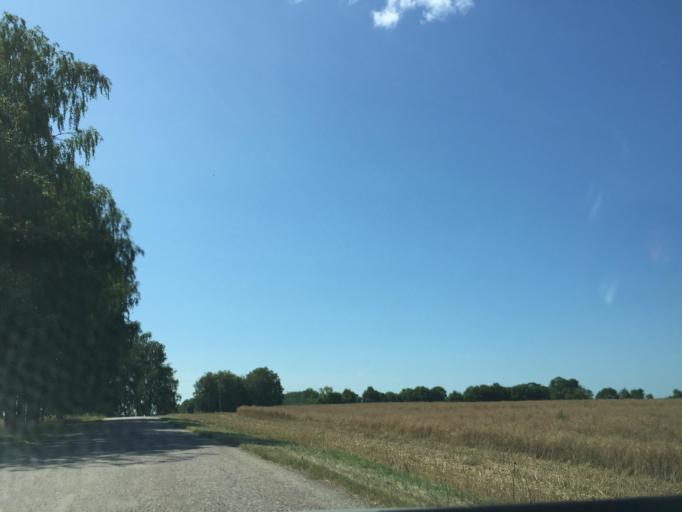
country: LV
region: Talsu Rajons
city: Talsi
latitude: 57.1477
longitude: 22.6738
